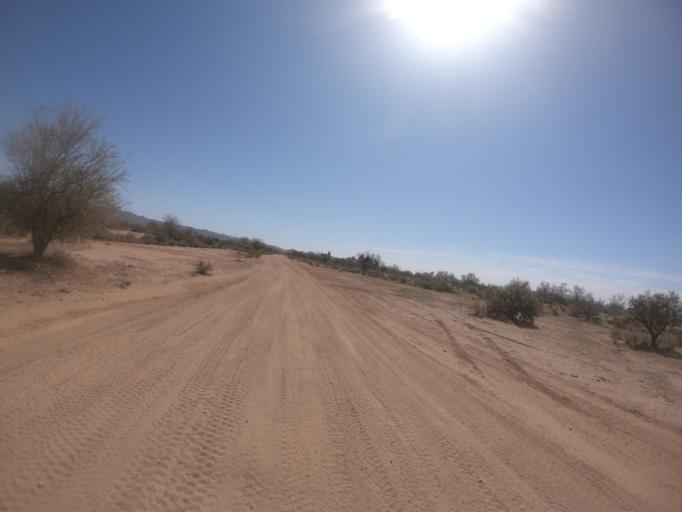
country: US
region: Arizona
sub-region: Pinal County
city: Gold Camp
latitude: 33.2370
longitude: -111.3077
